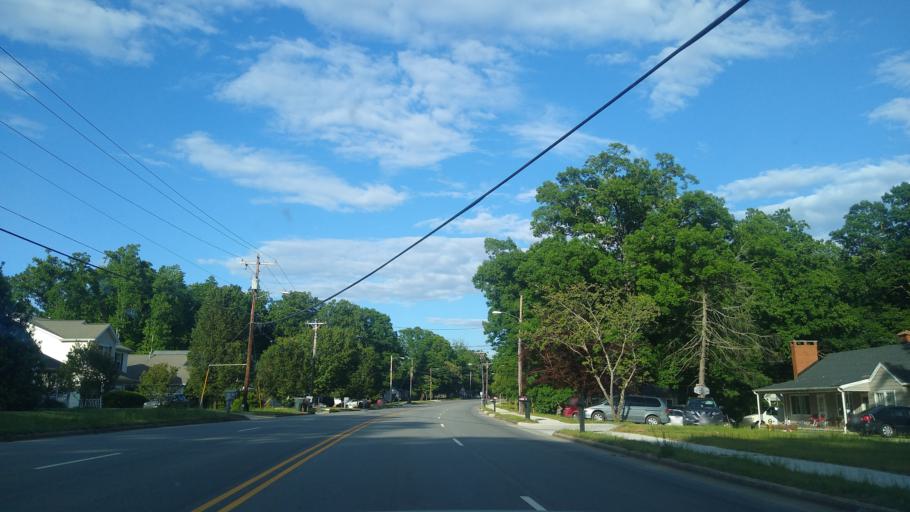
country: US
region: North Carolina
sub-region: Guilford County
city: Greensboro
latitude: 36.1440
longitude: -79.7669
